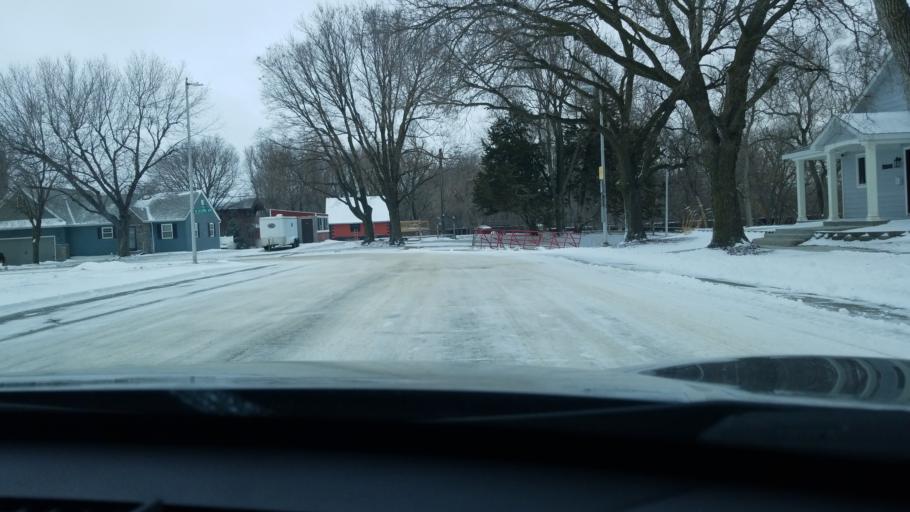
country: US
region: Iowa
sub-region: Lyon County
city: Rock Rapids
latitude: 43.4326
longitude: -96.1668
